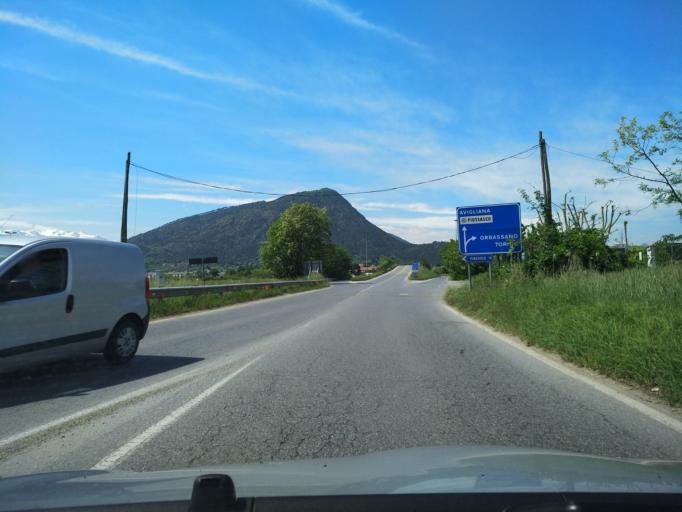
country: IT
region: Piedmont
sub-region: Provincia di Torino
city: Piossasco
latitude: 44.9768
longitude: 7.4762
